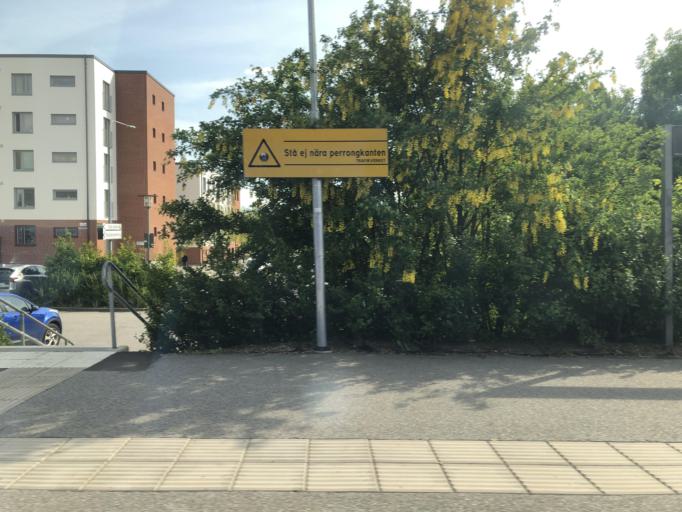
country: SE
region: Skane
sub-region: Malmo
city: Oxie
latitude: 55.5417
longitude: 13.0960
